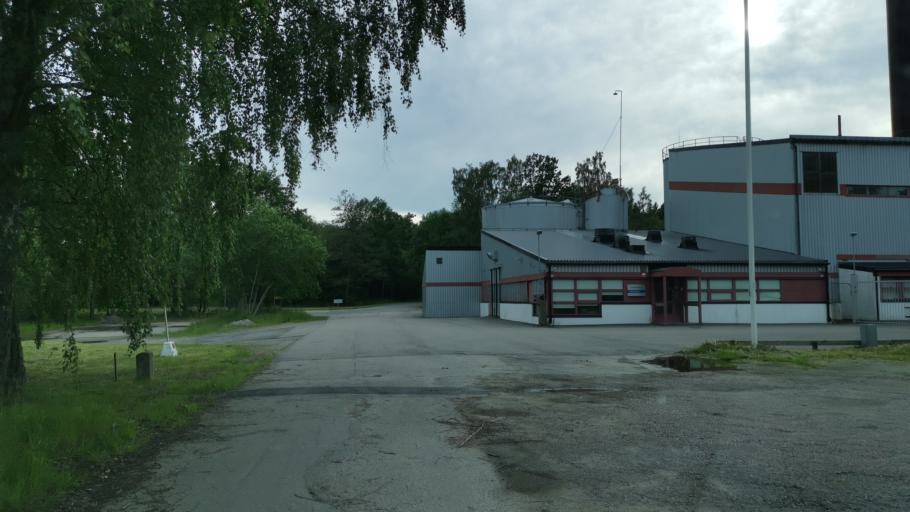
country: SE
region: Vaestra Goetaland
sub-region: Vanersborgs Kommun
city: Vargon
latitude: 58.3585
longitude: 12.3732
